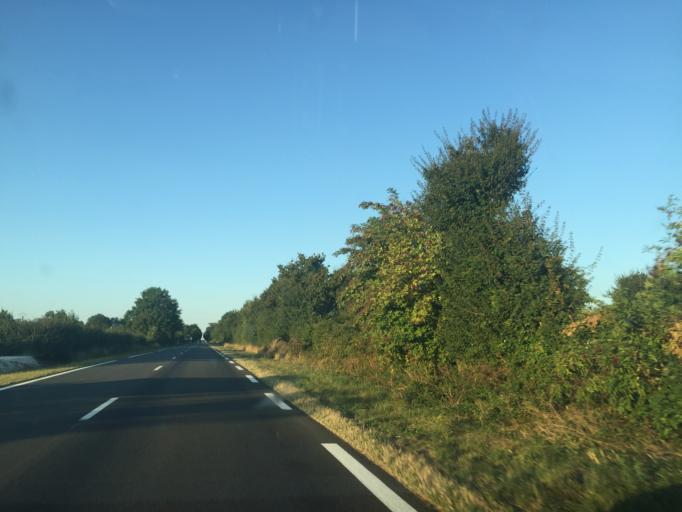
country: FR
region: Poitou-Charentes
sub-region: Departement de la Vienne
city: Rouille
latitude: 46.3981
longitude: 0.0682
